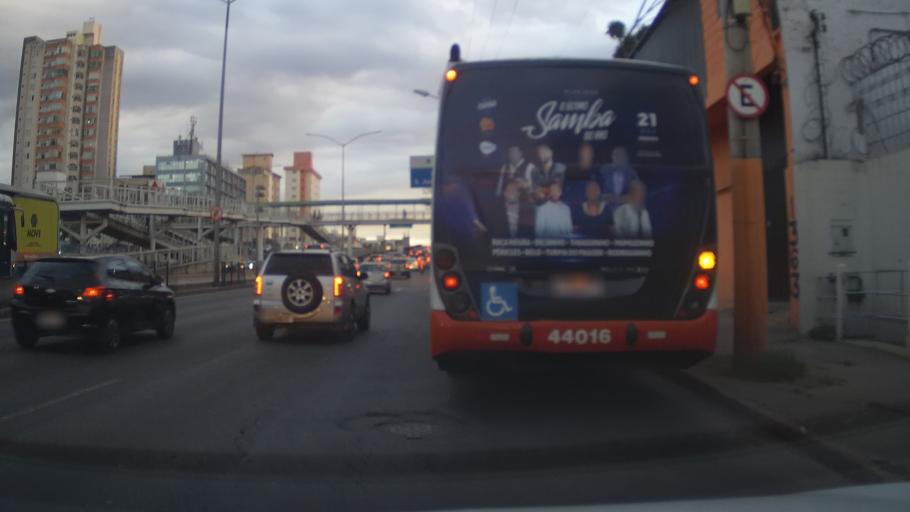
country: BR
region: Minas Gerais
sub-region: Belo Horizonte
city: Belo Horizonte
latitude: -19.8981
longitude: -43.9280
